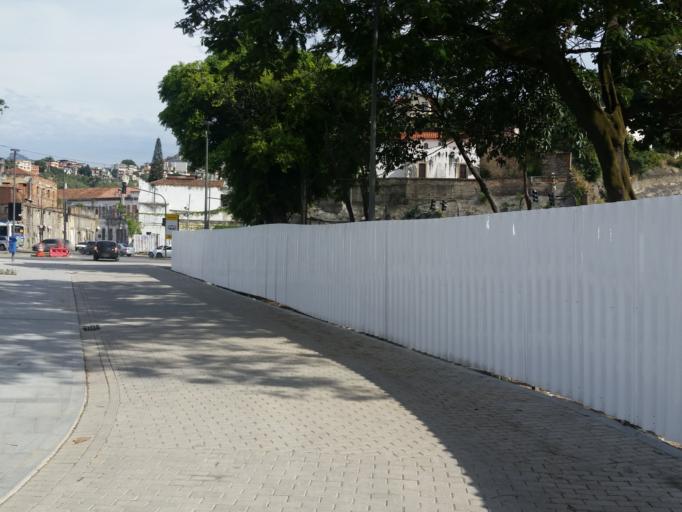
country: BR
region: Rio de Janeiro
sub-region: Rio De Janeiro
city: Rio de Janeiro
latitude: -22.8930
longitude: -43.1908
